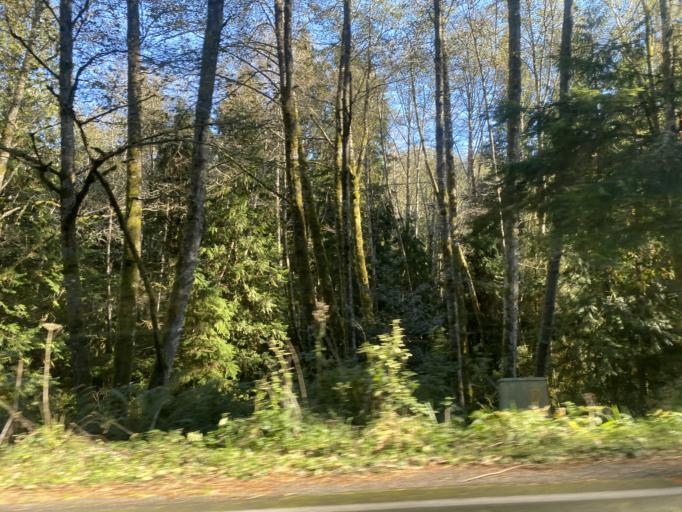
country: US
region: Washington
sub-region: Island County
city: Langley
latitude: 48.0341
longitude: -122.4220
